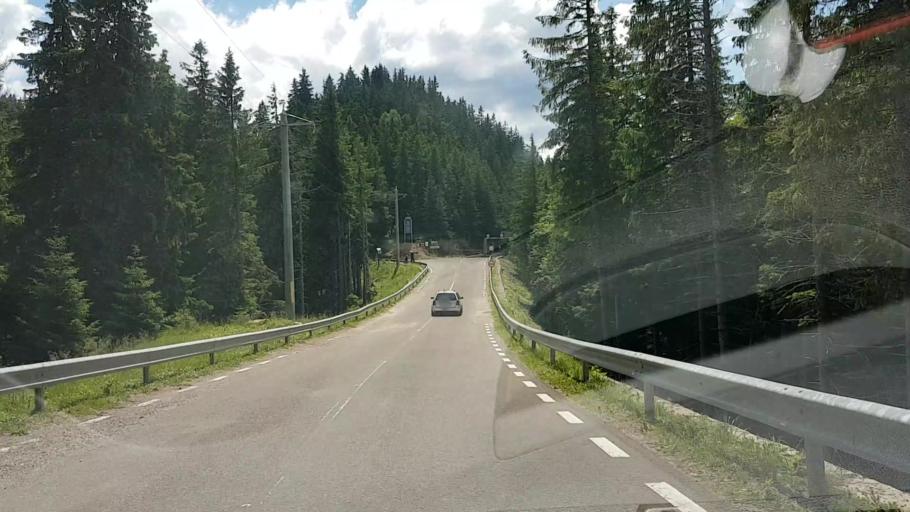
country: RO
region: Suceava
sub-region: Municipiul Campulung Moldovenesc
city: Campulung Moldovenesc
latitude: 47.4518
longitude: 25.5506
